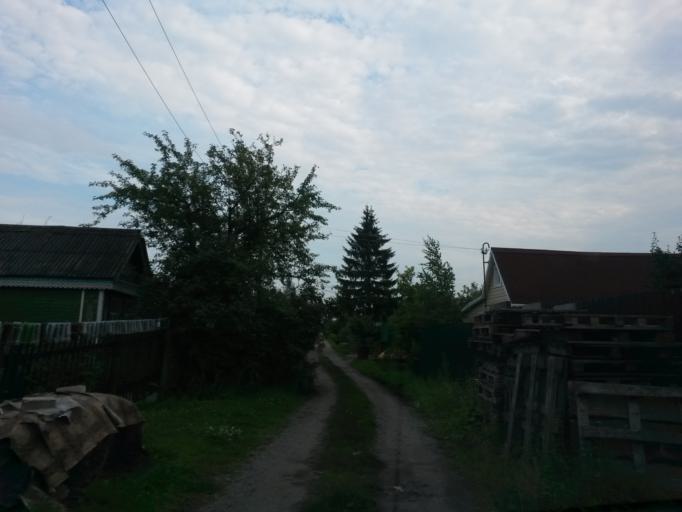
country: RU
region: Jaroslavl
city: Yaroslavl
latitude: 57.6100
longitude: 39.7840
